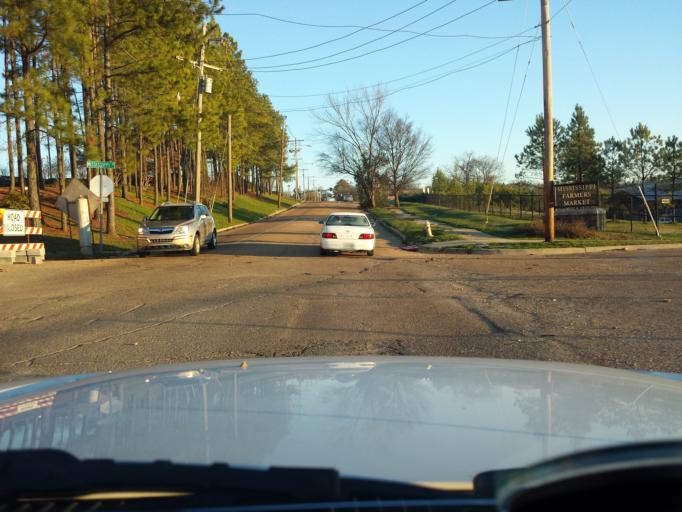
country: US
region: Mississippi
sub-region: Hinds County
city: Jackson
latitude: 32.3019
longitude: -90.1772
